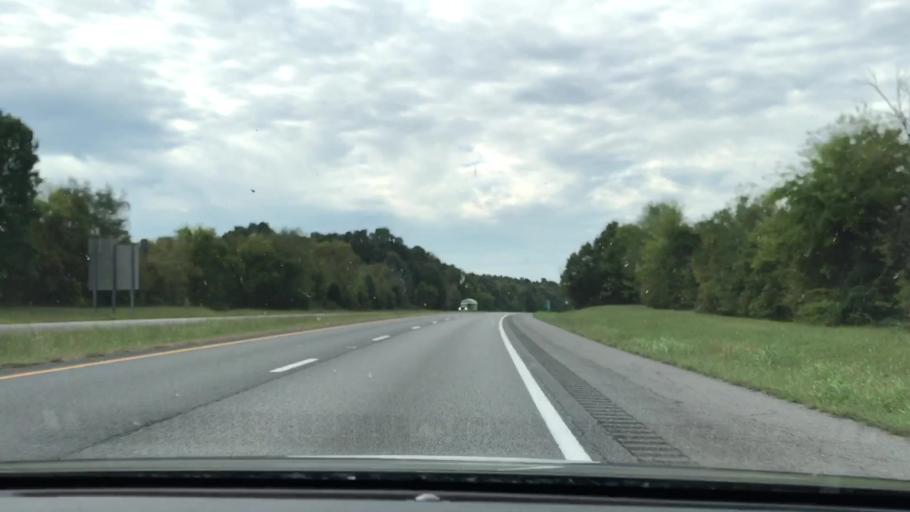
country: US
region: Kentucky
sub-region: Marshall County
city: Benton
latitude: 36.9008
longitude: -88.3475
